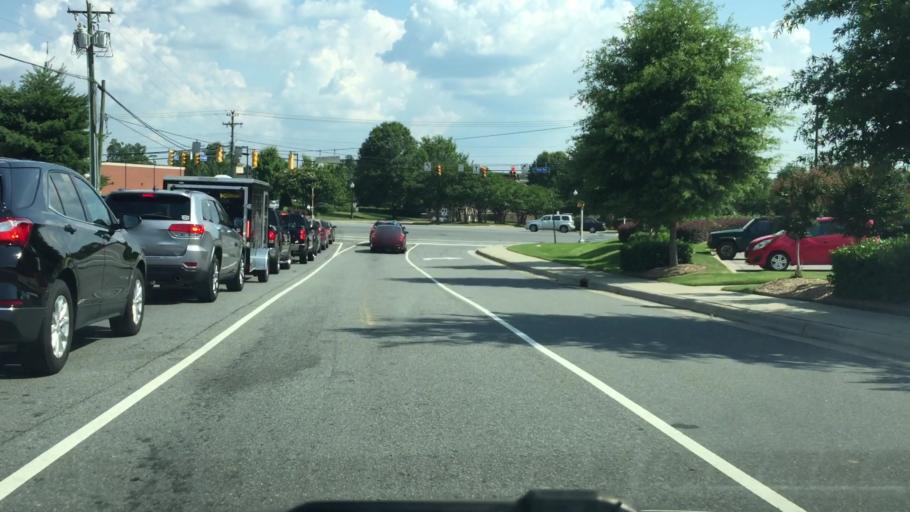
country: US
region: North Carolina
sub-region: Iredell County
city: Mooresville
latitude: 35.5968
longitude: -80.8775
